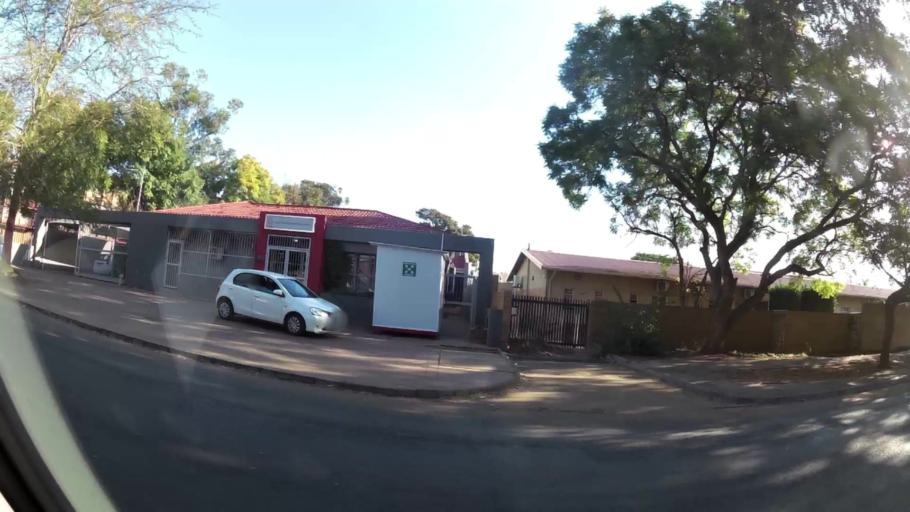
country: ZA
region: North-West
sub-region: Bojanala Platinum District Municipality
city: Rustenburg
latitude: -25.6725
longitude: 27.2392
